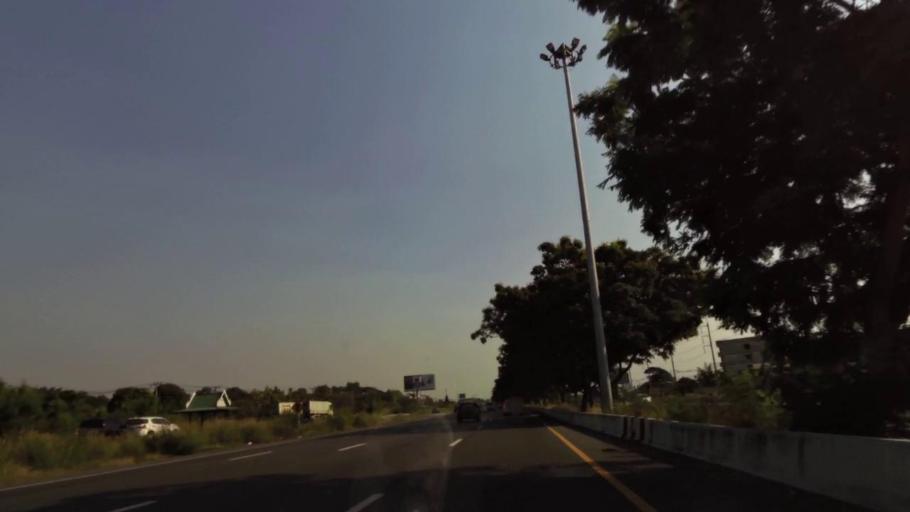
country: TH
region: Ang Thong
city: Ang Thong
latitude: 14.5764
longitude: 100.4871
